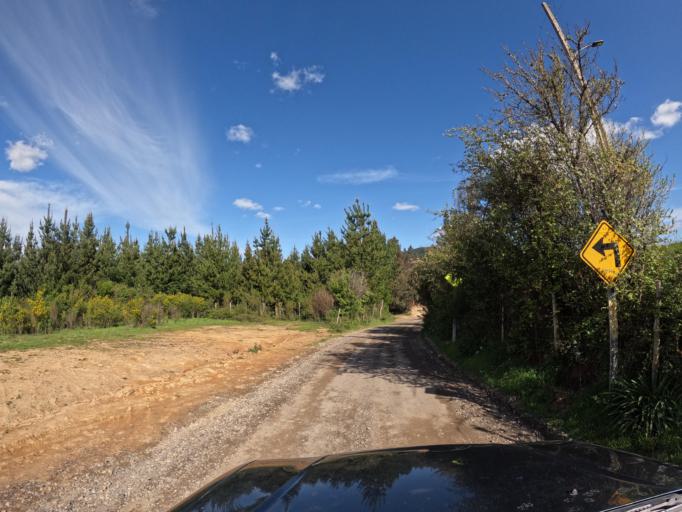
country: CL
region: Biobio
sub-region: Provincia de Concepcion
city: Chiguayante
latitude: -37.0635
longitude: -72.8889
